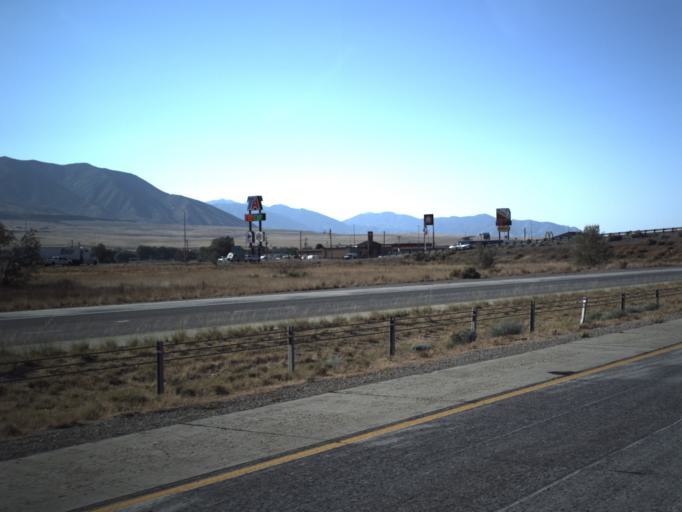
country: US
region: Utah
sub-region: Tooele County
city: Stansbury park
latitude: 40.6917
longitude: -112.2655
